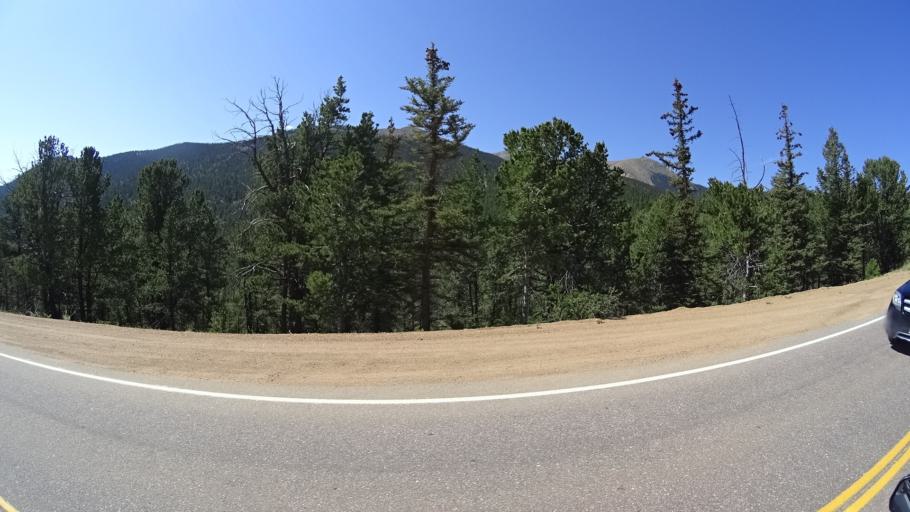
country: US
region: Colorado
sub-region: El Paso County
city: Cascade-Chipita Park
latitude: 38.9025
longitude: -105.0629
